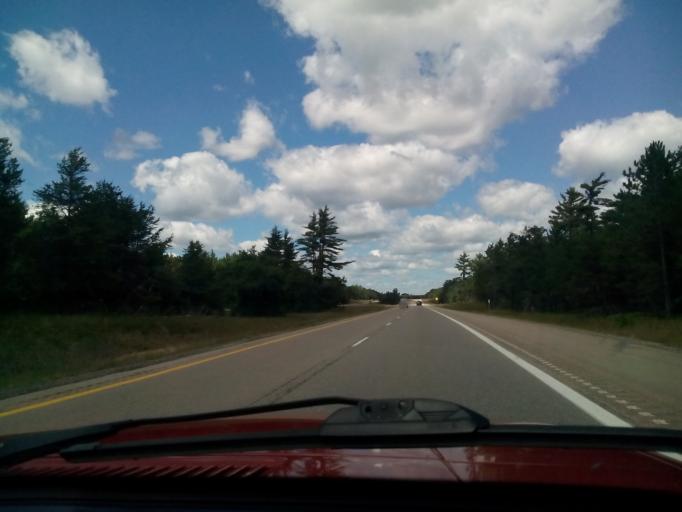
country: US
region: Michigan
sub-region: Crawford County
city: Grayling
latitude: 44.6615
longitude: -84.6972
